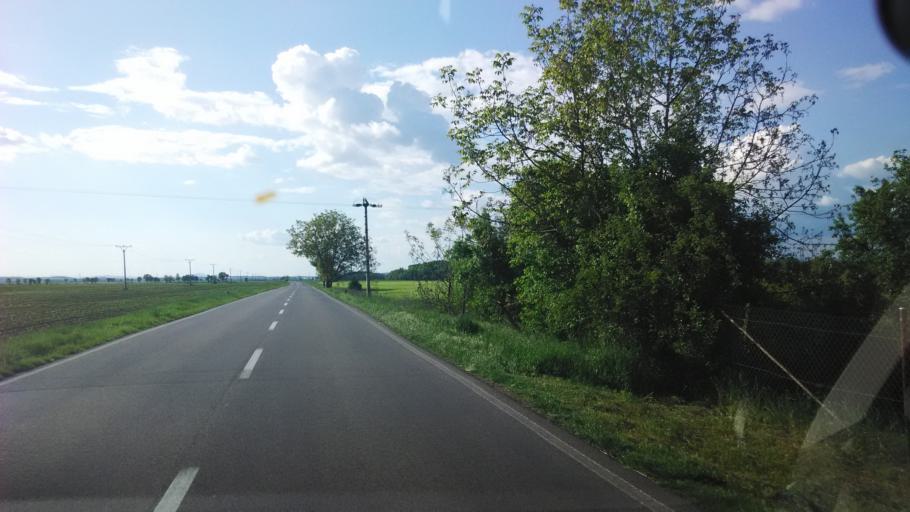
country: SK
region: Nitriansky
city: Levice
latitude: 48.1659
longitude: 18.5480
